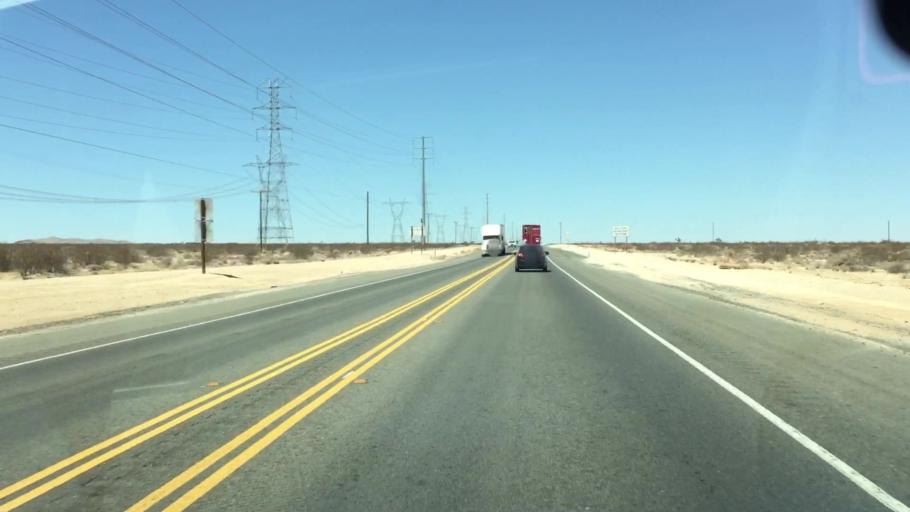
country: US
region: California
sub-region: San Bernardino County
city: Adelanto
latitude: 34.7000
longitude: -117.4533
